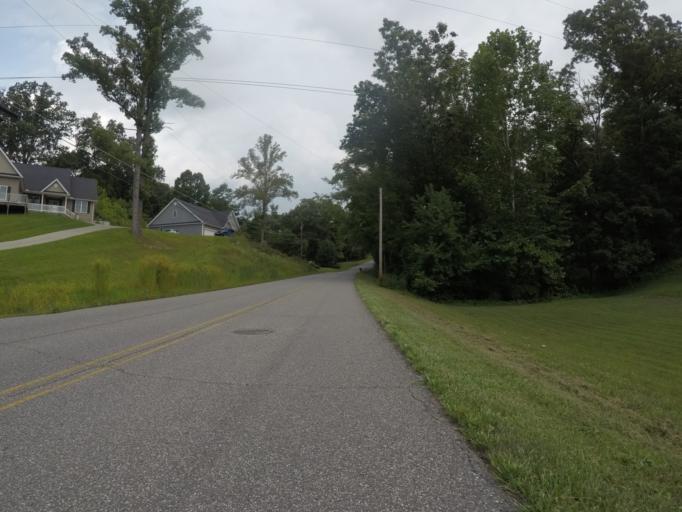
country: US
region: Kentucky
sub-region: Boyd County
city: Meads
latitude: 38.4191
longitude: -82.7075
